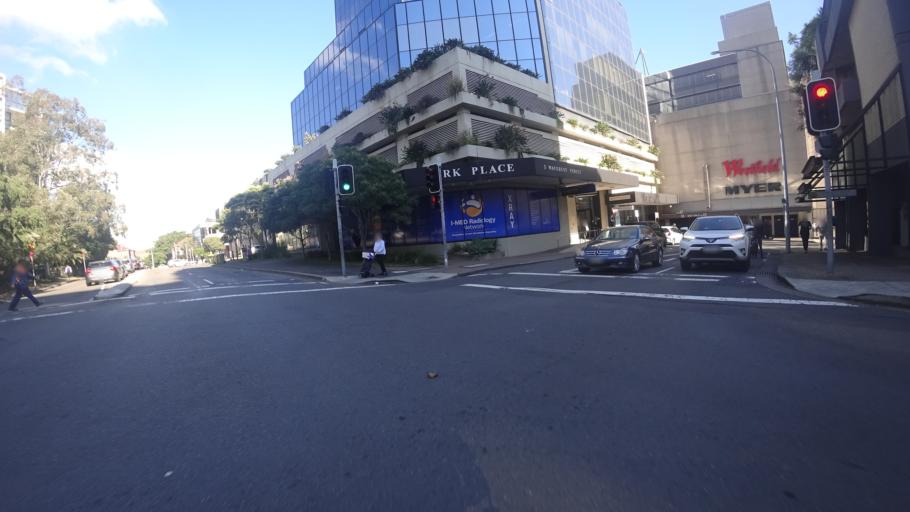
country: AU
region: New South Wales
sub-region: Waverley
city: Bondi Junction
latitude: -33.8926
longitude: 151.2519
